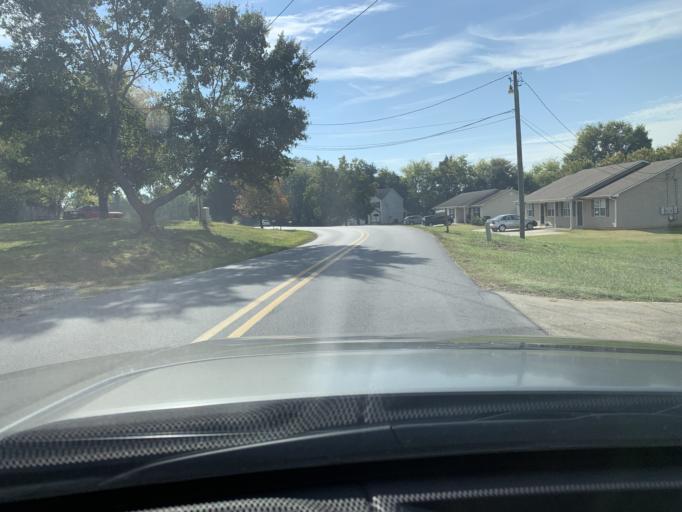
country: US
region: Georgia
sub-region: Polk County
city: Aragon
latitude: 34.0371
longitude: -85.0504
